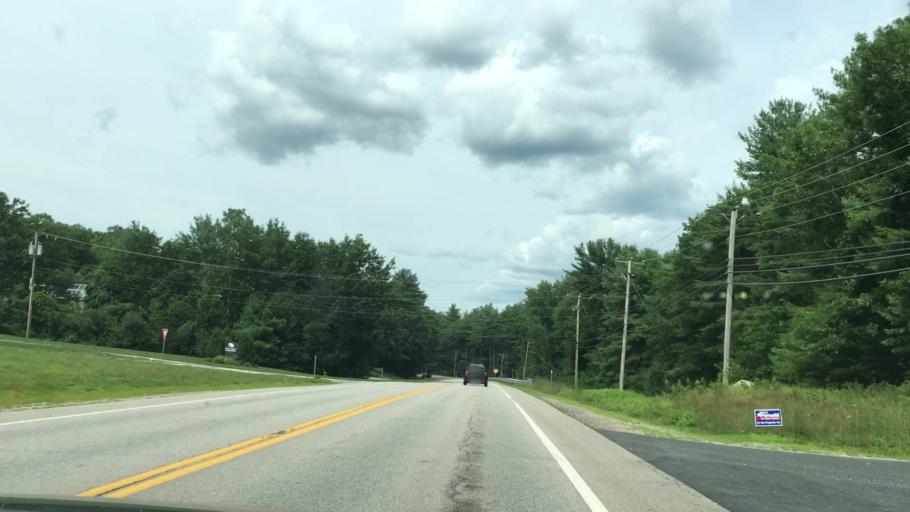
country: US
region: New Hampshire
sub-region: Hillsborough County
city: Peterborough
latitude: 42.8436
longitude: -71.9663
